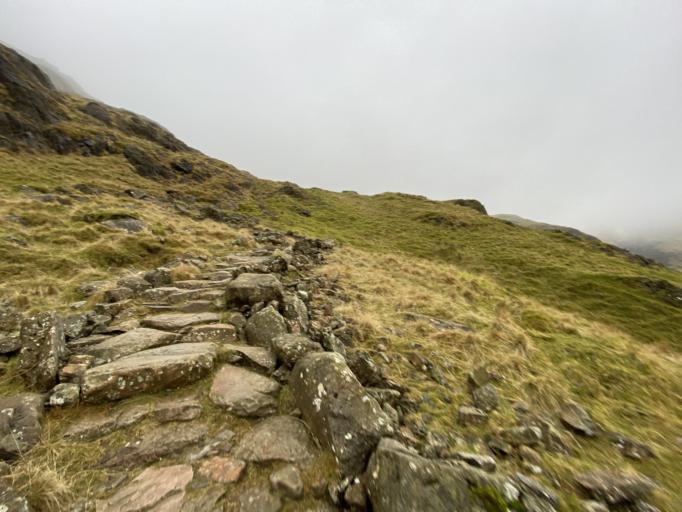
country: GB
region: England
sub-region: Cumbria
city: Keswick
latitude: 54.4696
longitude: -3.2040
